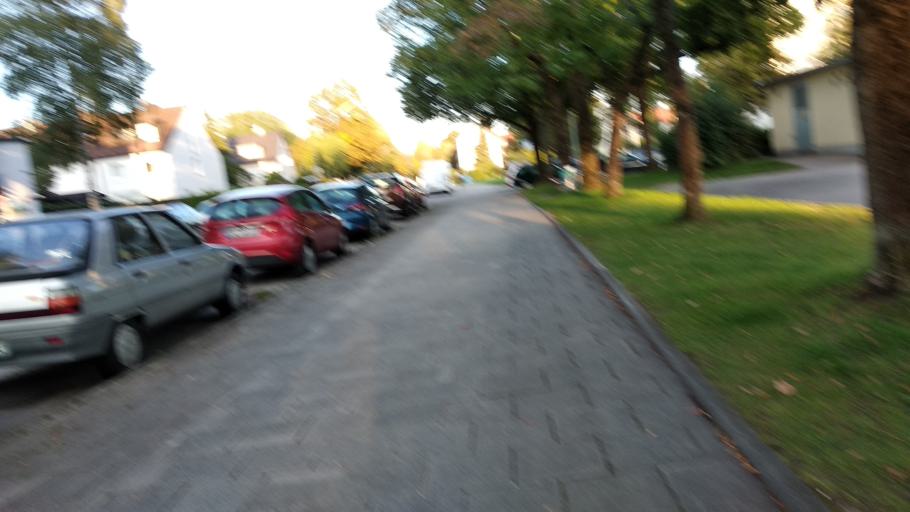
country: DE
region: Bavaria
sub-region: Upper Bavaria
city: Bogenhausen
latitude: 48.1302
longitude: 11.6336
